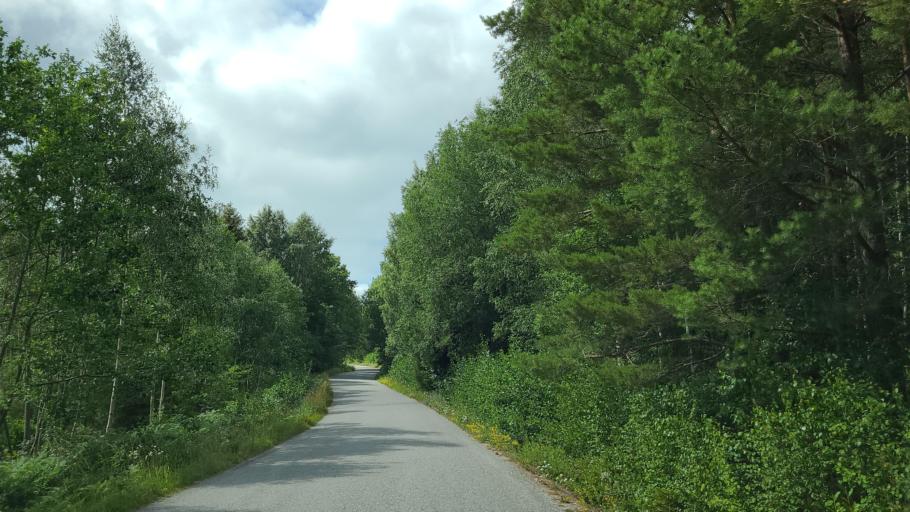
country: FI
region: Varsinais-Suomi
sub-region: Aboland-Turunmaa
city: Nagu
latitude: 60.1637
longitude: 22.0272
